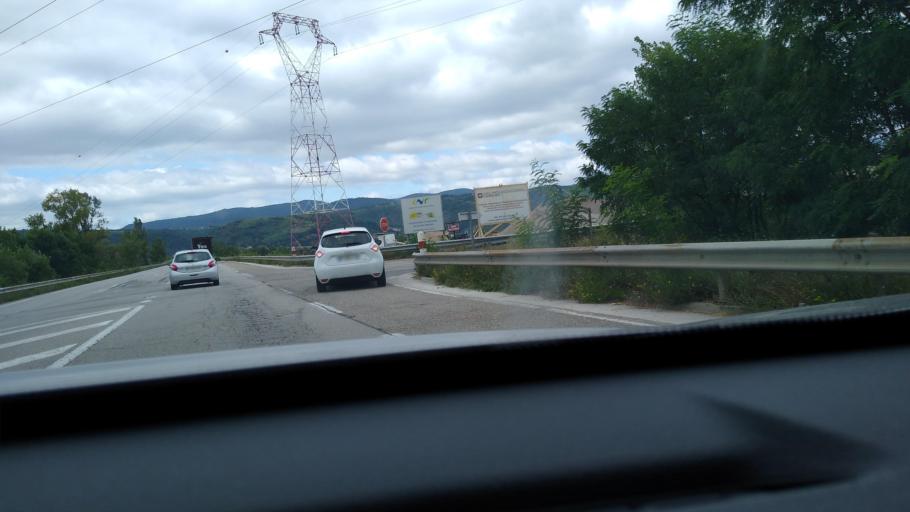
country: FR
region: Rhone-Alpes
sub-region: Departement de l'Isere
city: Sablons
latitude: 45.3176
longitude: 4.7957
